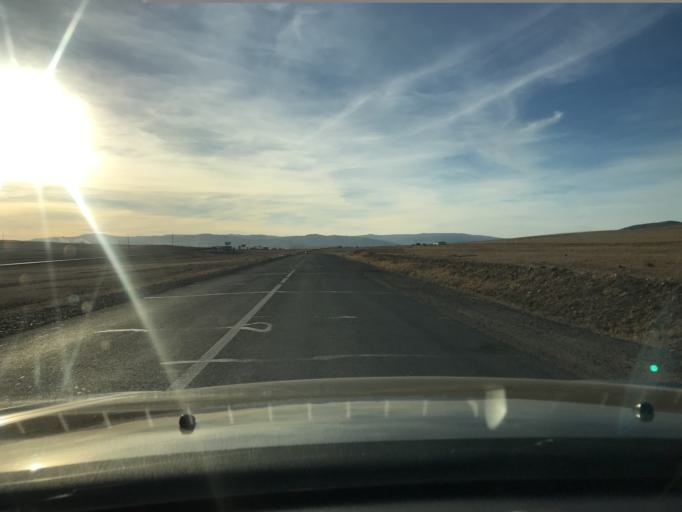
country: MN
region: Central Aimak
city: Dzuunmod
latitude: 47.7883
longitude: 107.3119
